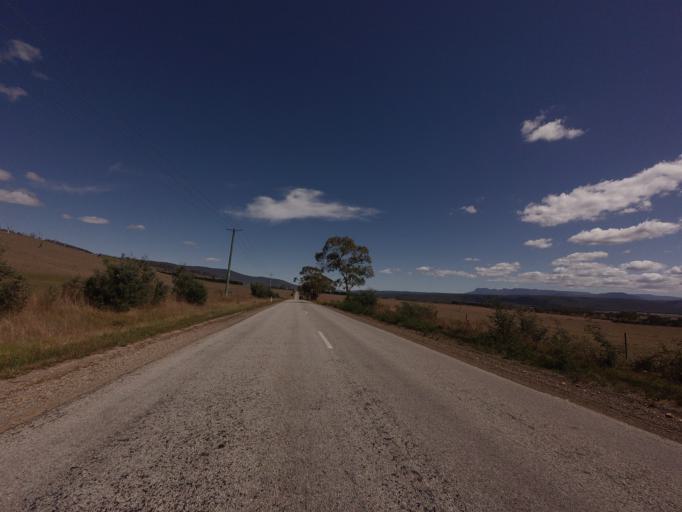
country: AU
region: Tasmania
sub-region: Break O'Day
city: St Helens
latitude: -41.6114
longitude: 148.0175
